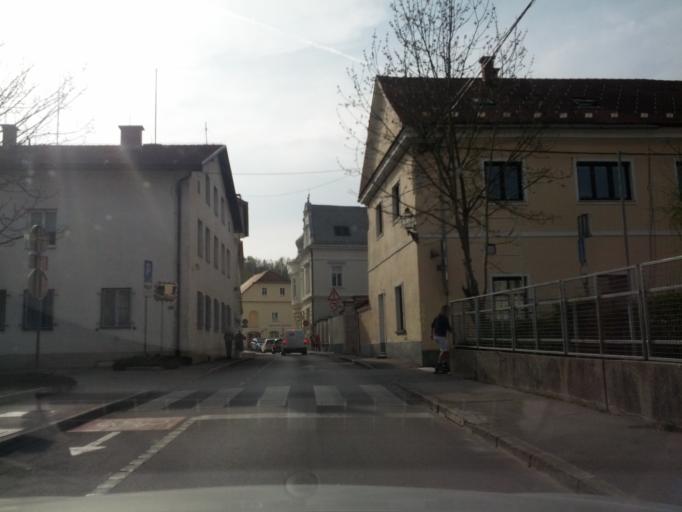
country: SI
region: Kamnik
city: Kamnik
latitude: 46.2270
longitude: 14.6132
